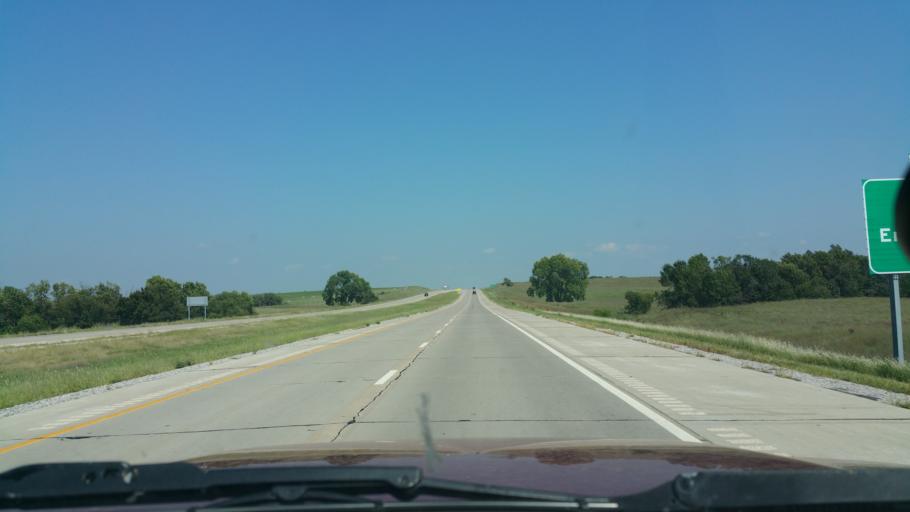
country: US
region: Kansas
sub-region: Dickinson County
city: Abilene
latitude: 38.9520
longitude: -97.1269
